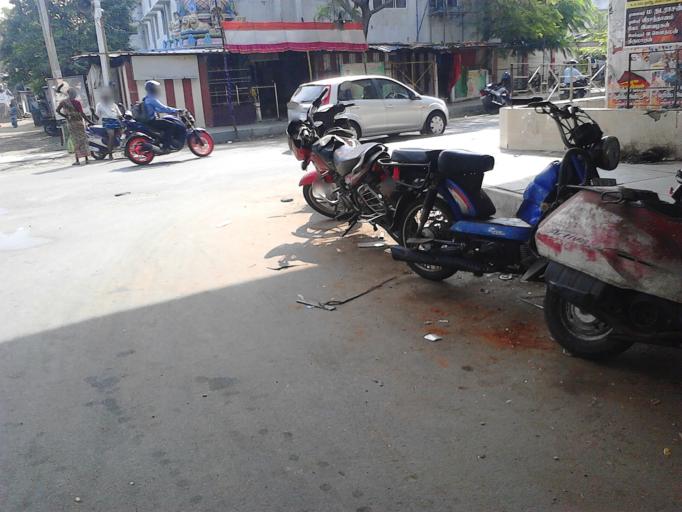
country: IN
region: Tamil Nadu
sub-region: Kancheepuram
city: Alandur
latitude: 13.0095
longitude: 80.2037
